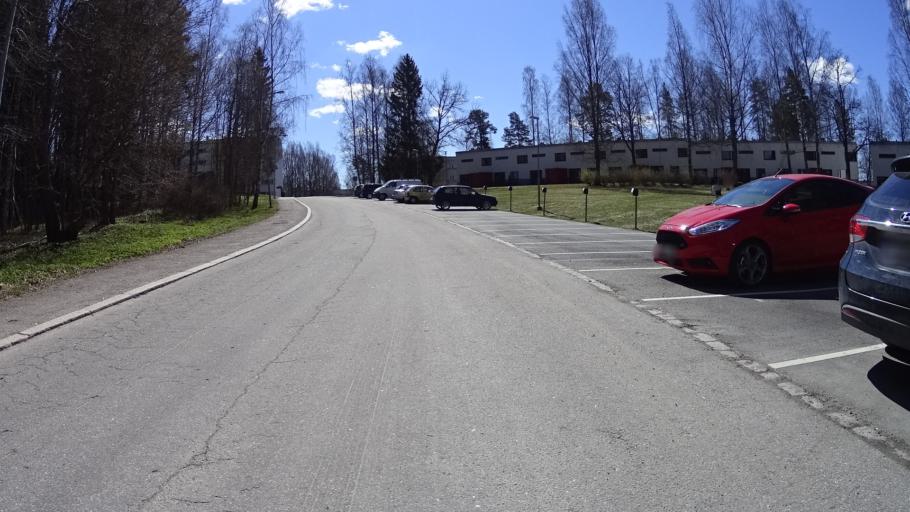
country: FI
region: Uusimaa
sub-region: Helsinki
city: Kauniainen
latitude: 60.2437
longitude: 24.7395
